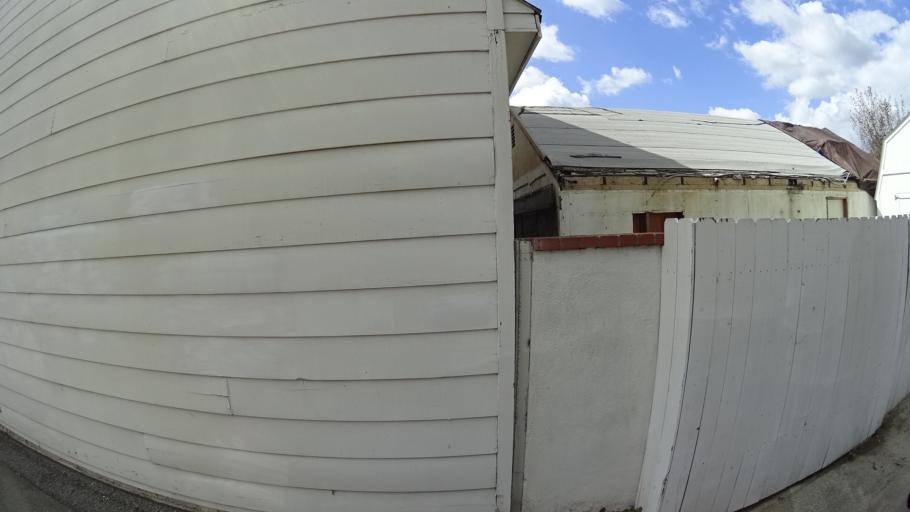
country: US
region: California
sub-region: Orange County
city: Anaheim
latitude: 33.8414
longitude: -117.9200
